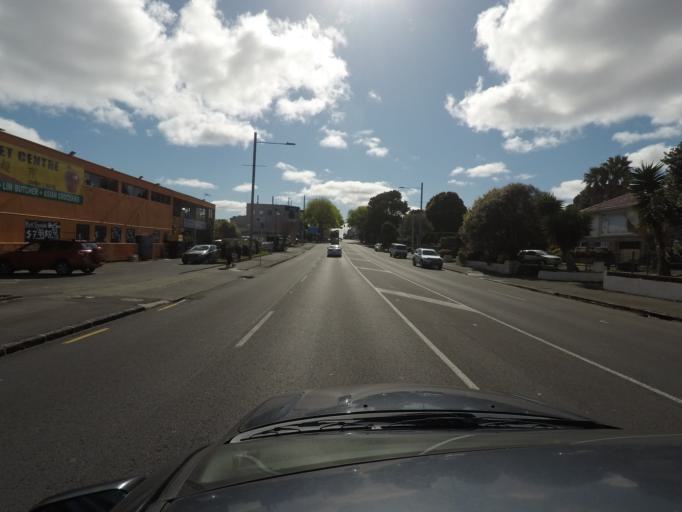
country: NZ
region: Auckland
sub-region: Auckland
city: Rosebank
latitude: -36.8867
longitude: 174.7129
